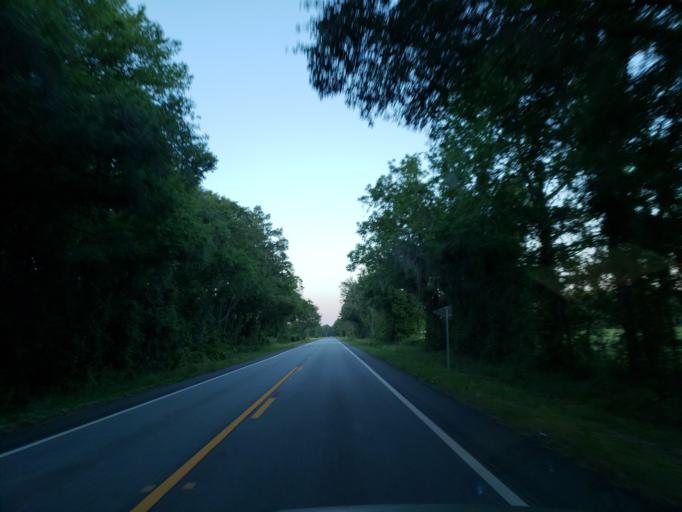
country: US
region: Florida
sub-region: Hamilton County
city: Jasper
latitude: 30.5547
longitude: -83.0754
